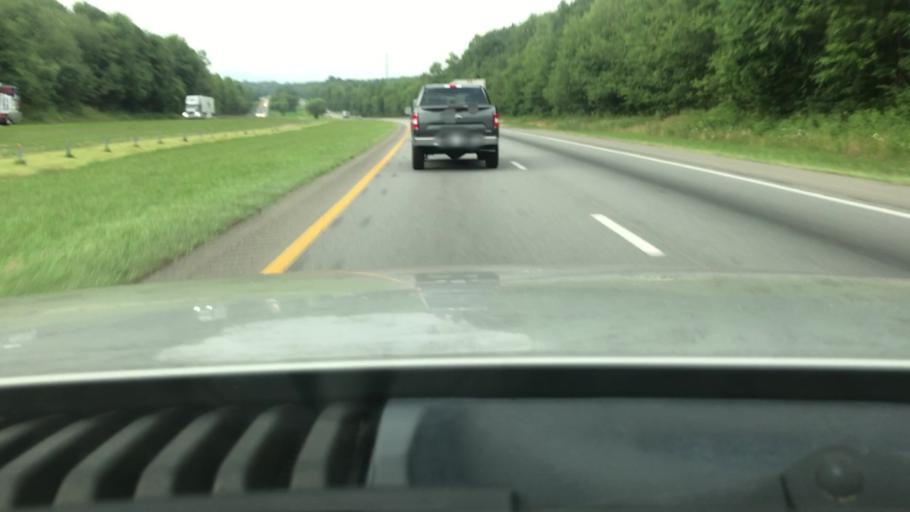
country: US
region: North Carolina
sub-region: Surry County
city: Dobson
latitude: 36.3296
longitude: -80.7938
